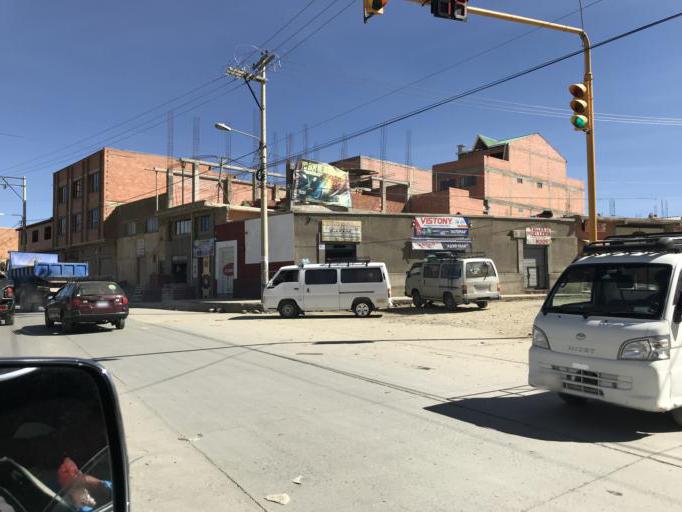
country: BO
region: La Paz
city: La Paz
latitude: -16.4852
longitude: -68.2104
